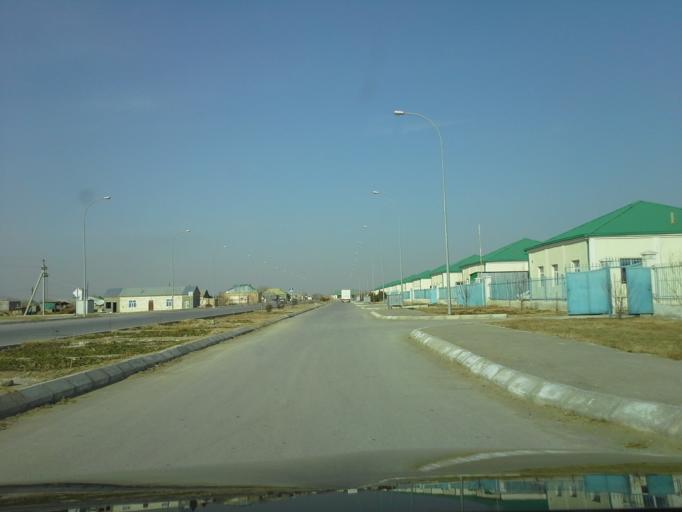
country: TM
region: Ahal
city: Abadan
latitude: 38.1717
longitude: 58.0470
